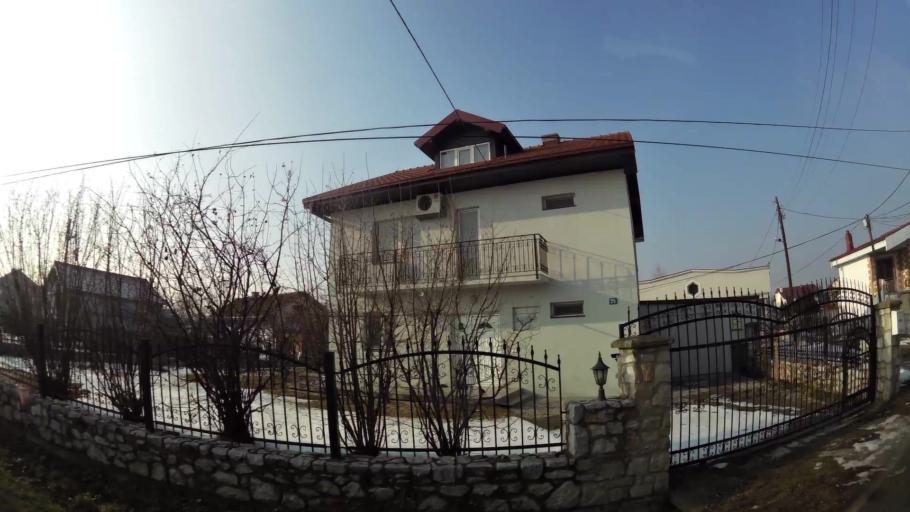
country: MK
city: Kadino
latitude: 41.9552
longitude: 21.6011
